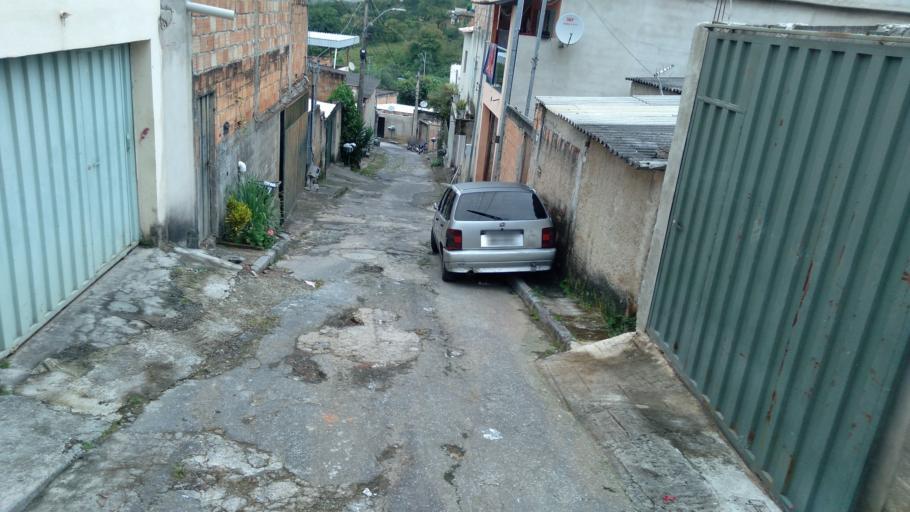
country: BR
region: Minas Gerais
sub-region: Santa Luzia
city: Santa Luzia
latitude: -19.8320
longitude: -43.8682
